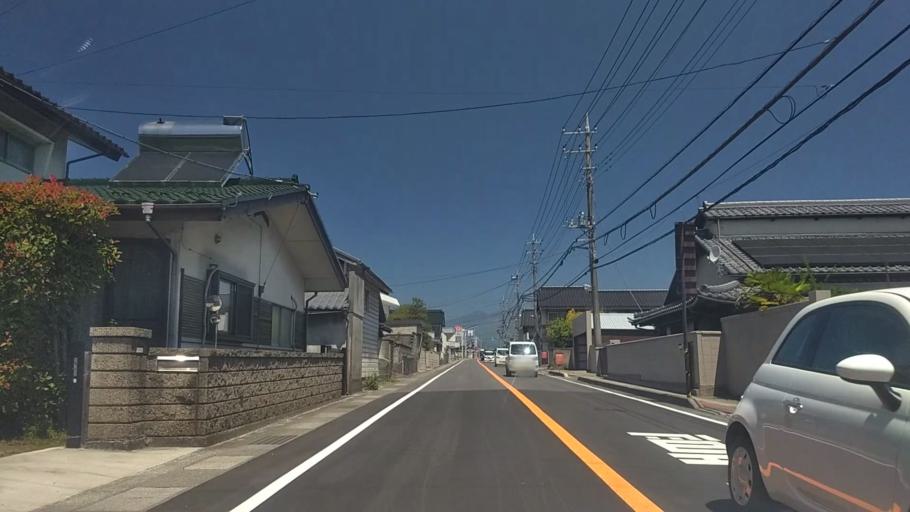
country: JP
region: Yamanashi
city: Nirasaki
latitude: 35.7298
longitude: 138.4483
